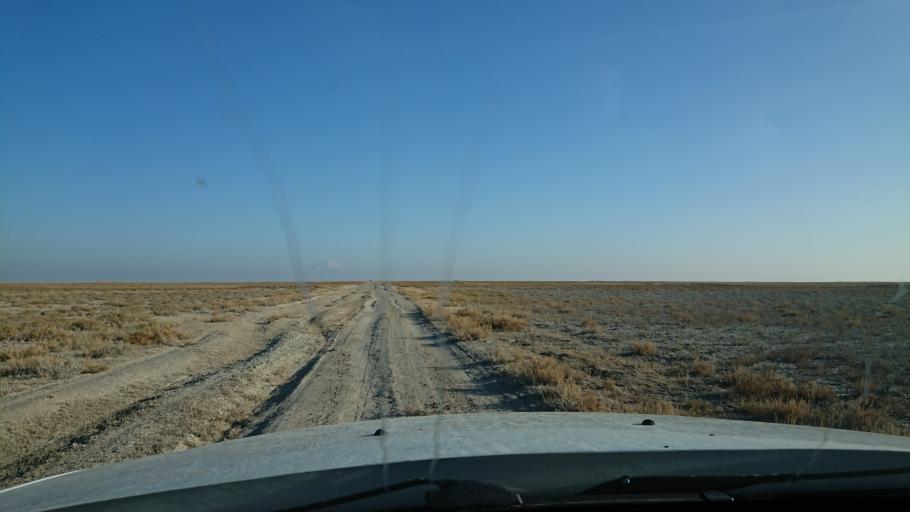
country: TR
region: Aksaray
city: Eskil
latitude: 38.4062
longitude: 33.5712
